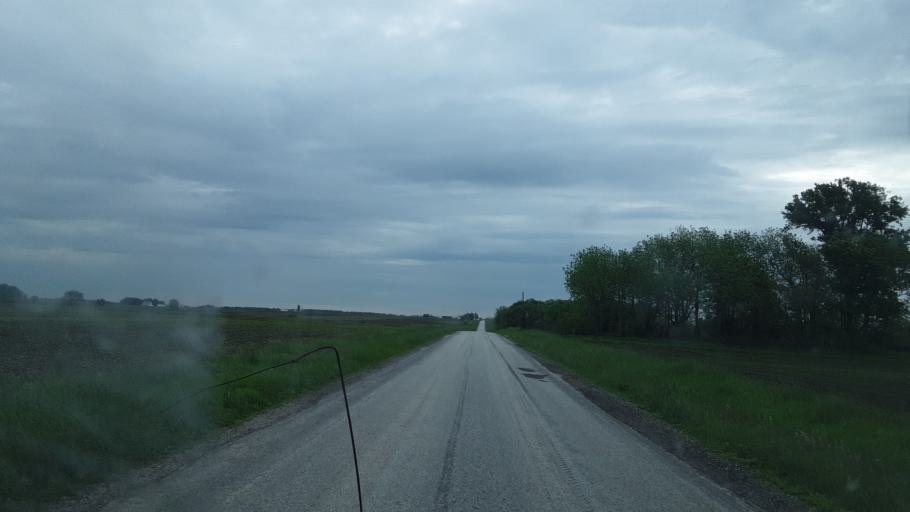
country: US
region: Illinois
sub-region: McDonough County
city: Macomb
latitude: 40.3818
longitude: -90.6509
